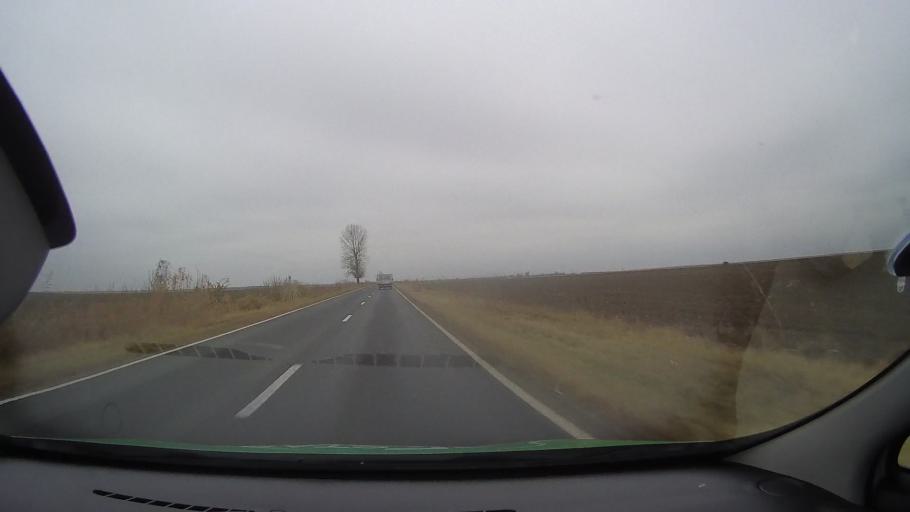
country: RO
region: Ialomita
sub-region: Comuna Scanteia
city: Scanteia
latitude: 44.7462
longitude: 27.4453
